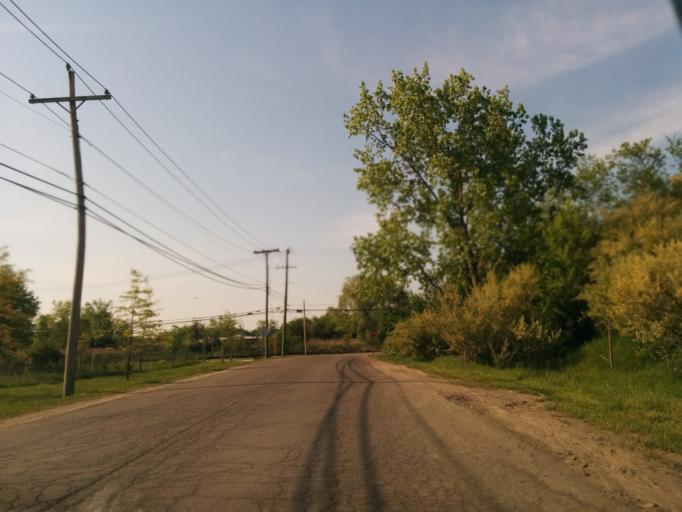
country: US
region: Michigan
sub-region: Oakland County
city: Novi
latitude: 42.4821
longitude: -83.4645
